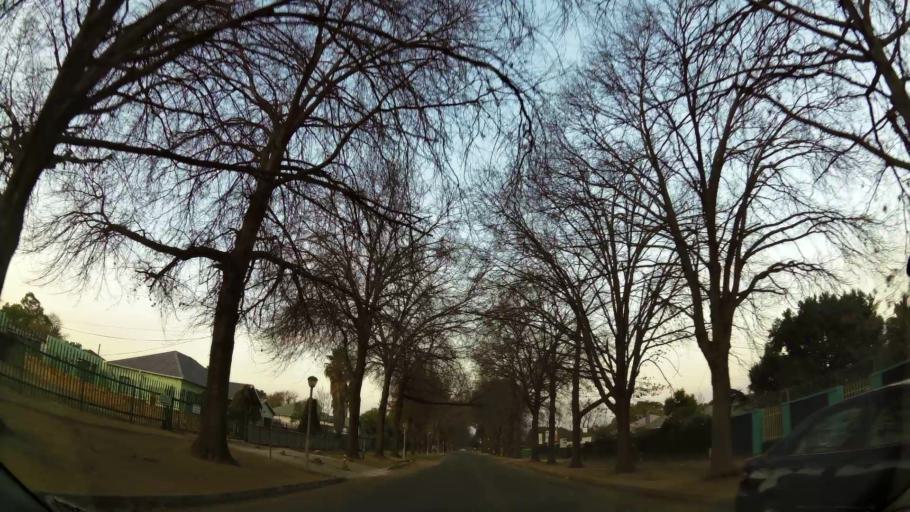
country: ZA
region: Gauteng
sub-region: Ekurhuleni Metropolitan Municipality
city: Benoni
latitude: -26.1735
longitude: 28.3188
